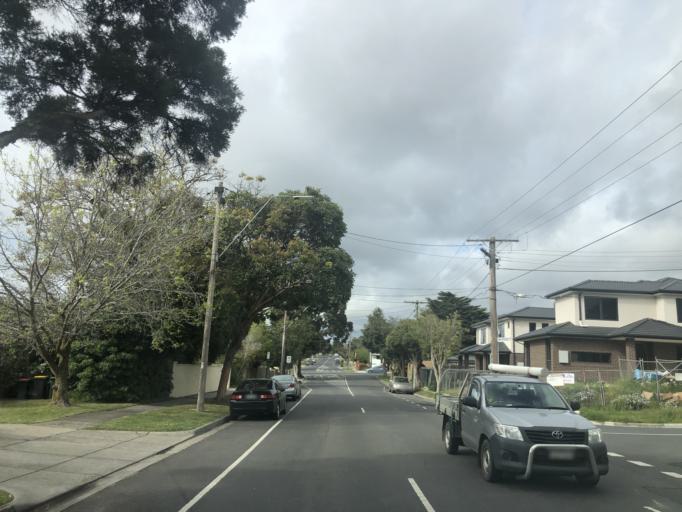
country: AU
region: Victoria
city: Burwood East
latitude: -37.8704
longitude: 145.1424
